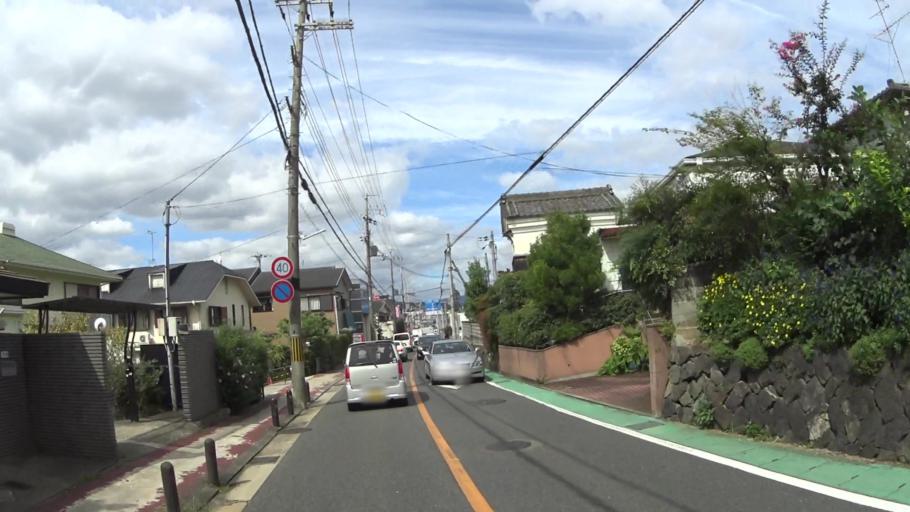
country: JP
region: Kyoto
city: Uji
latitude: 34.9239
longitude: 135.7996
